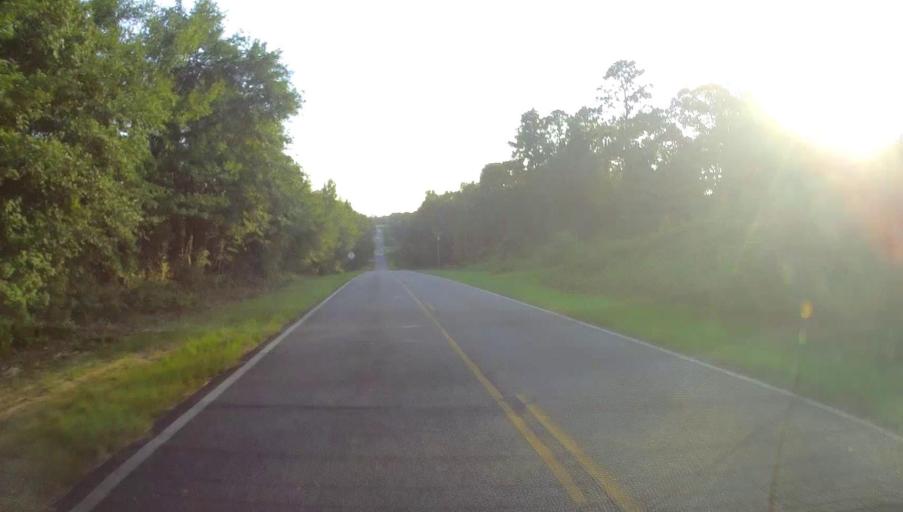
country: US
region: Georgia
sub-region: Peach County
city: Byron
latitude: 32.6262
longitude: -83.8193
